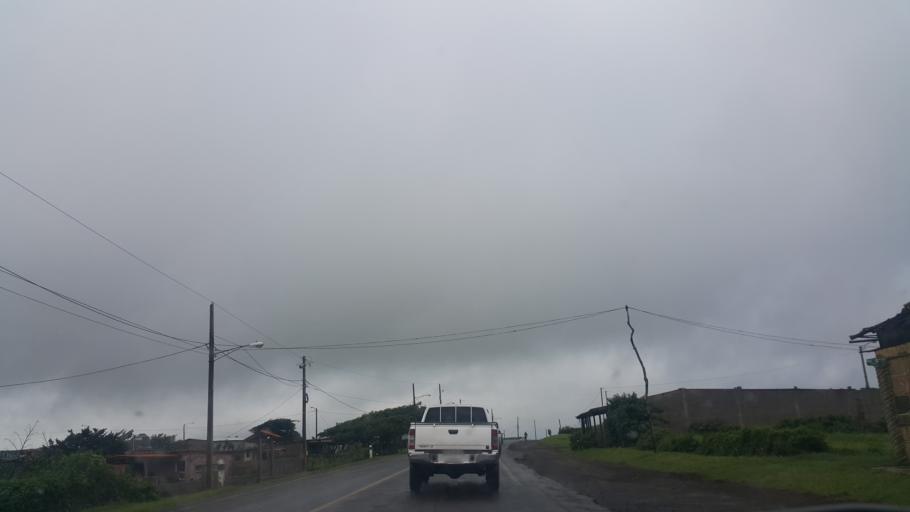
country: NI
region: Managua
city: El Crucero
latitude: 11.9575
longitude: -86.3030
